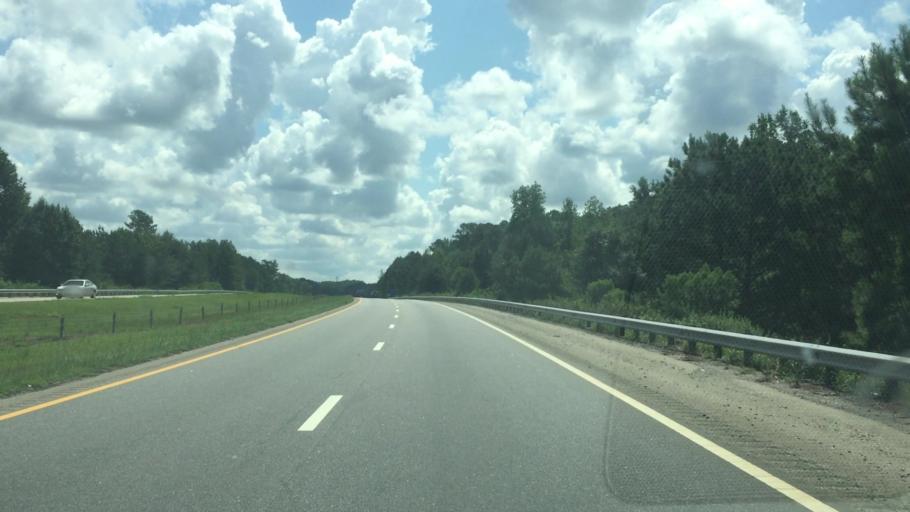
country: US
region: North Carolina
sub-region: Richmond County
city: Cordova
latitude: 34.9205
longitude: -79.8116
